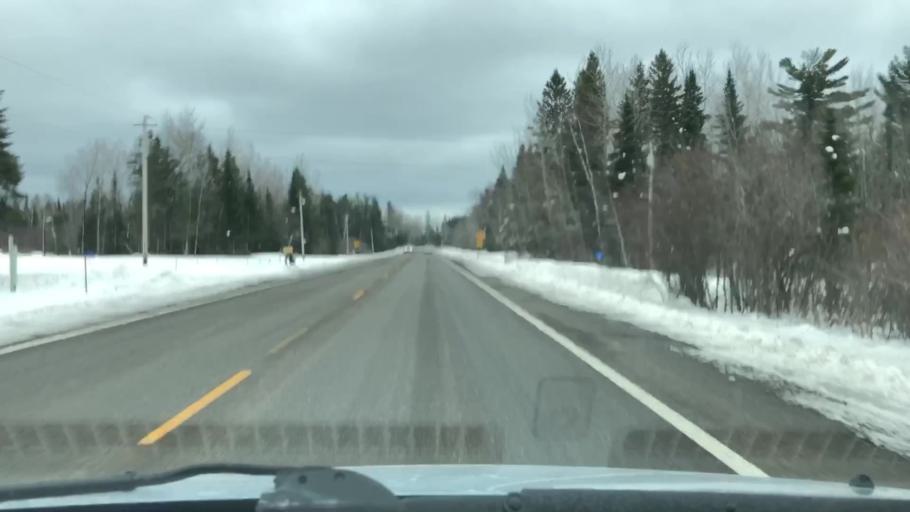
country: US
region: Minnesota
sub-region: Carlton County
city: Esko
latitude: 46.6881
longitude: -92.3648
